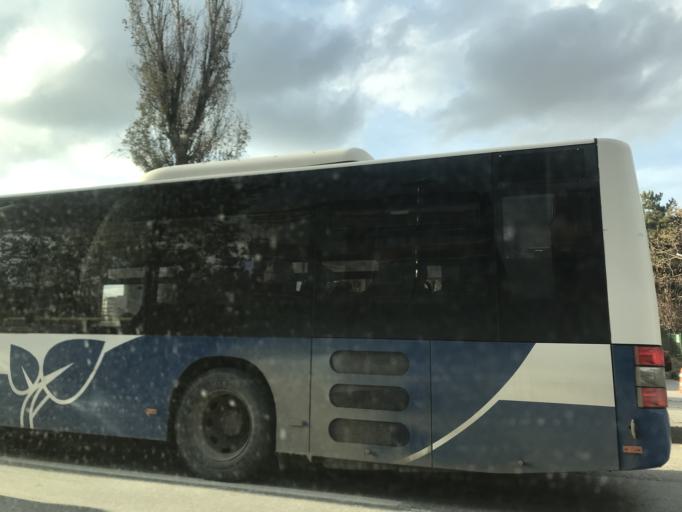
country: TR
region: Ankara
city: Mamak
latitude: 39.9646
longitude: 32.8715
